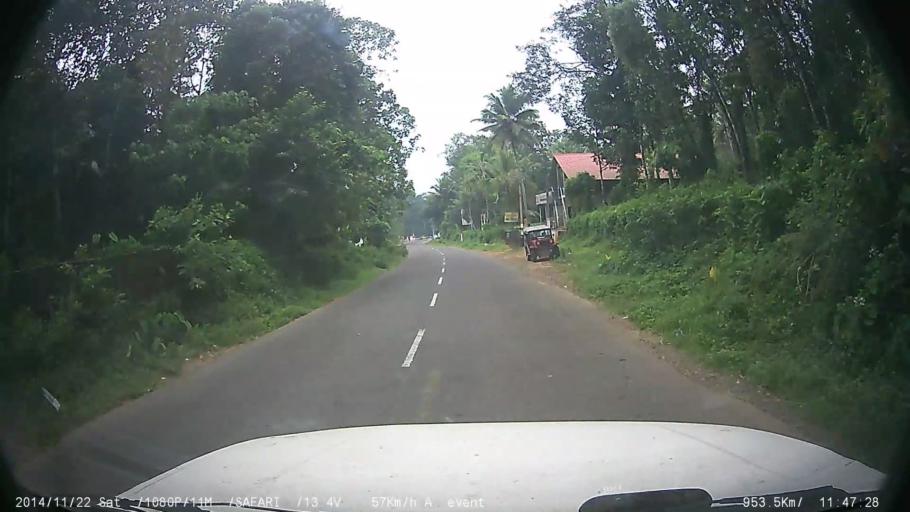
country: IN
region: Kerala
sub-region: Kottayam
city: Palackattumala
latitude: 9.8334
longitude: 76.5924
